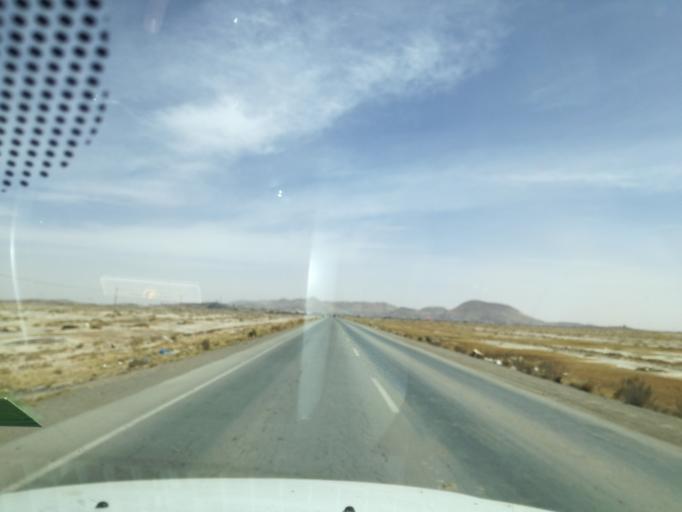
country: BO
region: Oruro
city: Oruro
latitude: -17.9050
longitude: -67.0569
